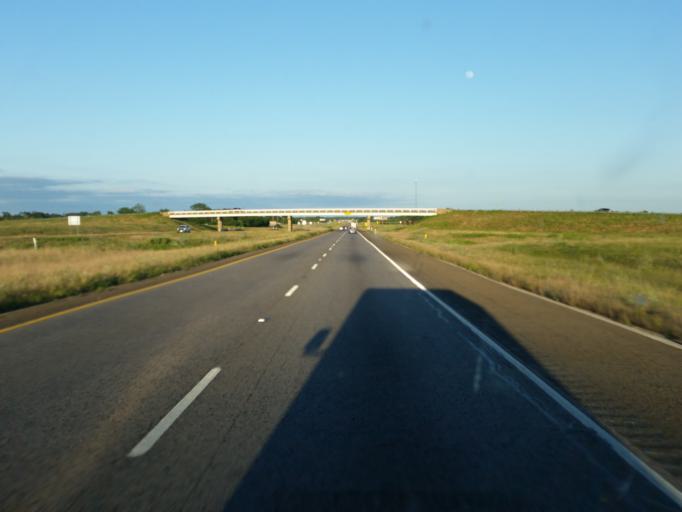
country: US
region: Texas
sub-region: Van Zandt County
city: Wills Point
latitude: 32.6559
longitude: -96.0968
